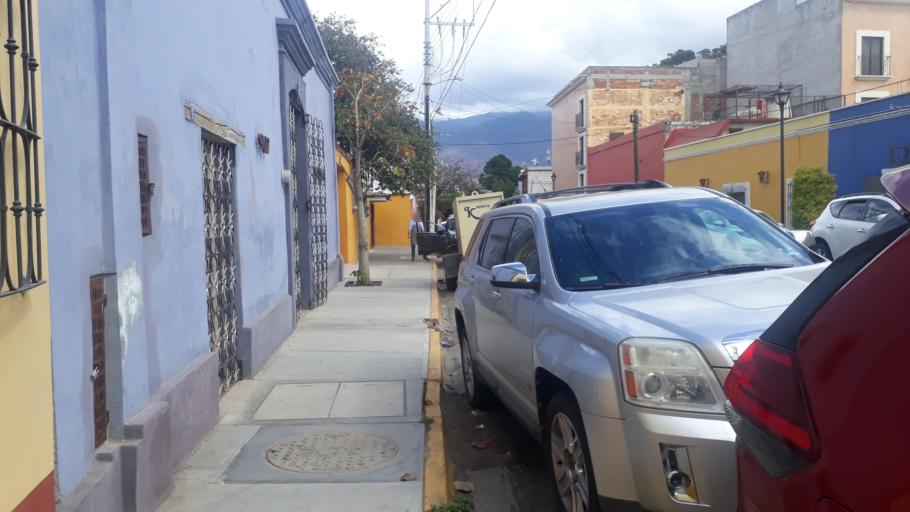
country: MX
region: Oaxaca
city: Oaxaca de Juarez
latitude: 17.0706
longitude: -96.7229
